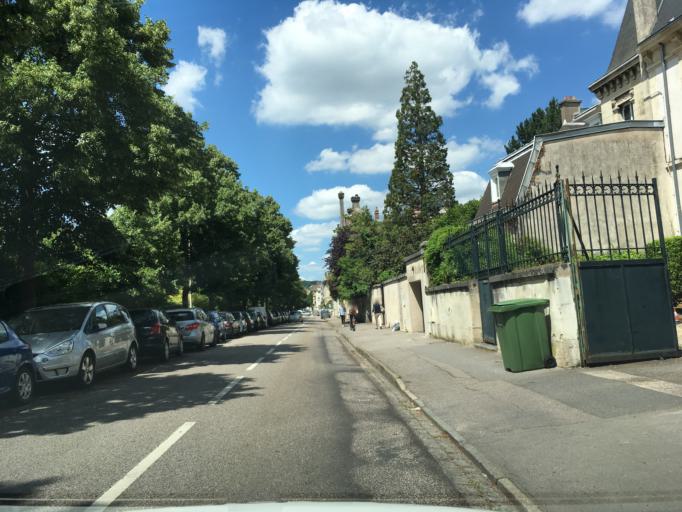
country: FR
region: Lorraine
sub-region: Departement de Meurthe-et-Moselle
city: Maxeville
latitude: 48.6979
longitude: 6.1702
